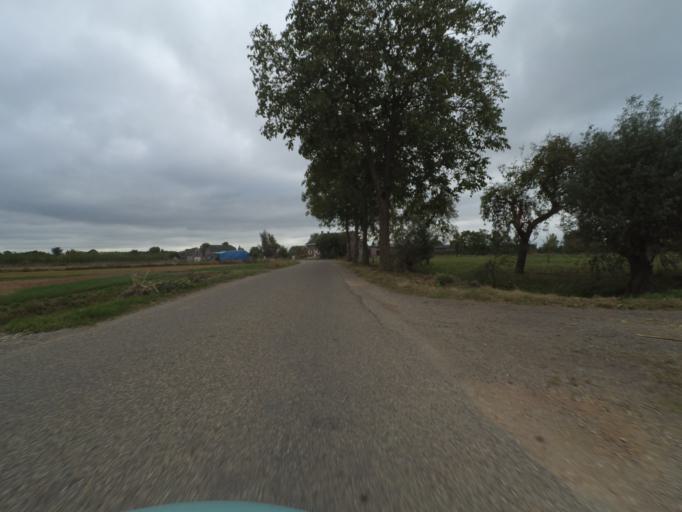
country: NL
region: Gelderland
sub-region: Gemeente Buren
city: Lienden
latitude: 51.9568
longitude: 5.5121
